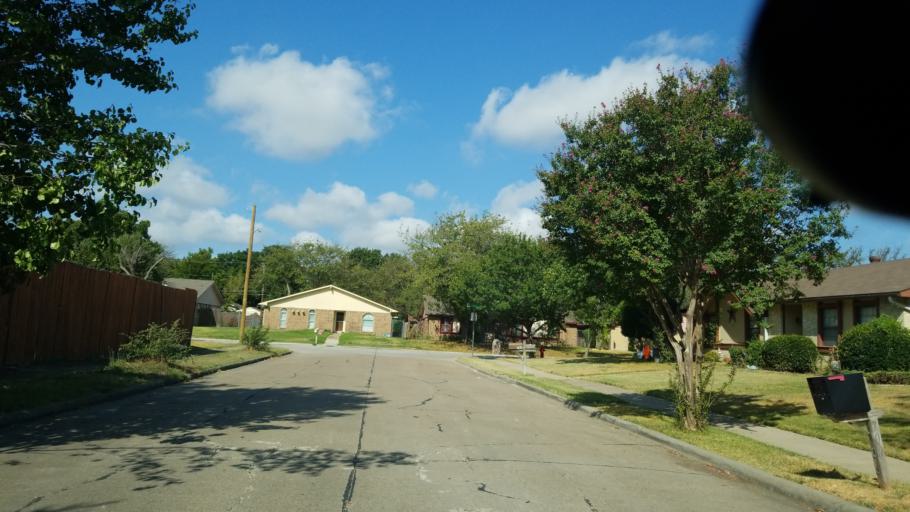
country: US
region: Texas
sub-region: Dallas County
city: Grand Prairie
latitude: 32.6977
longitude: -96.9973
